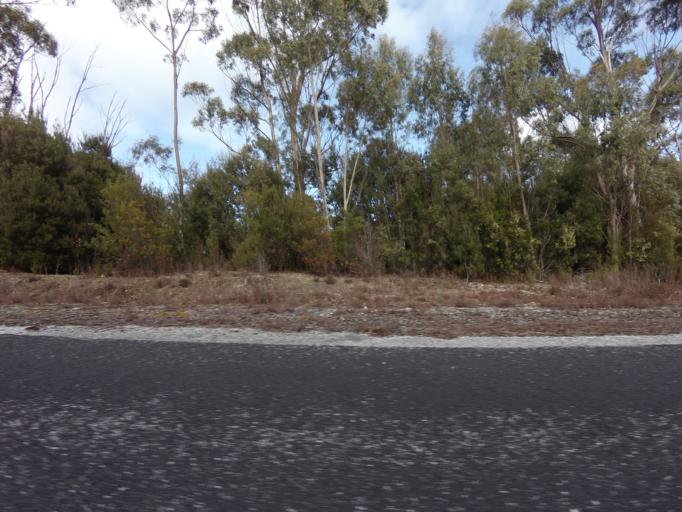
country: AU
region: Tasmania
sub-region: West Coast
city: Queenstown
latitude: -42.8053
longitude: 146.0956
